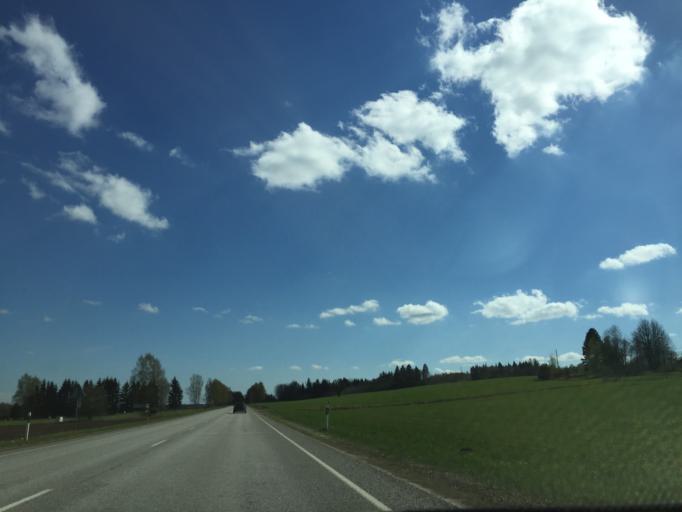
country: EE
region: Valgamaa
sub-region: Valga linn
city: Valga
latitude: 57.8961
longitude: 26.0526
